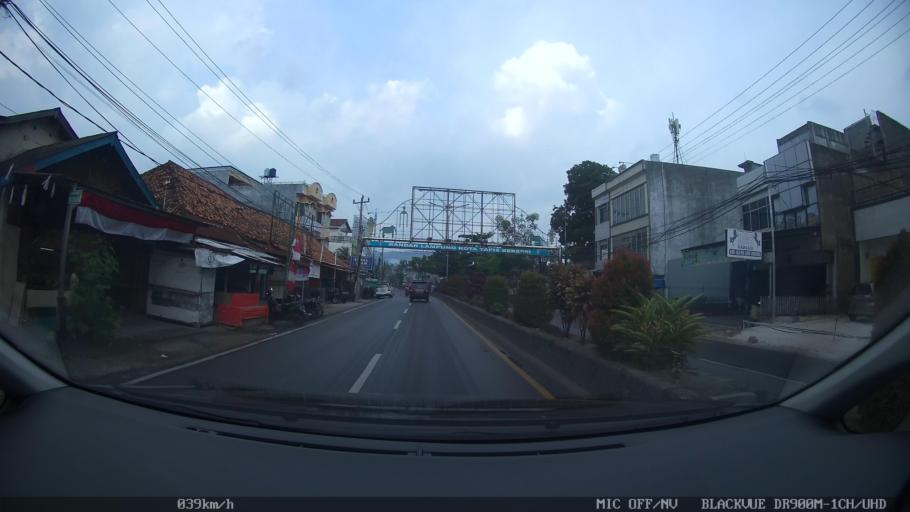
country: ID
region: Lampung
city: Bandarlampung
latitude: -5.4458
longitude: 105.2760
